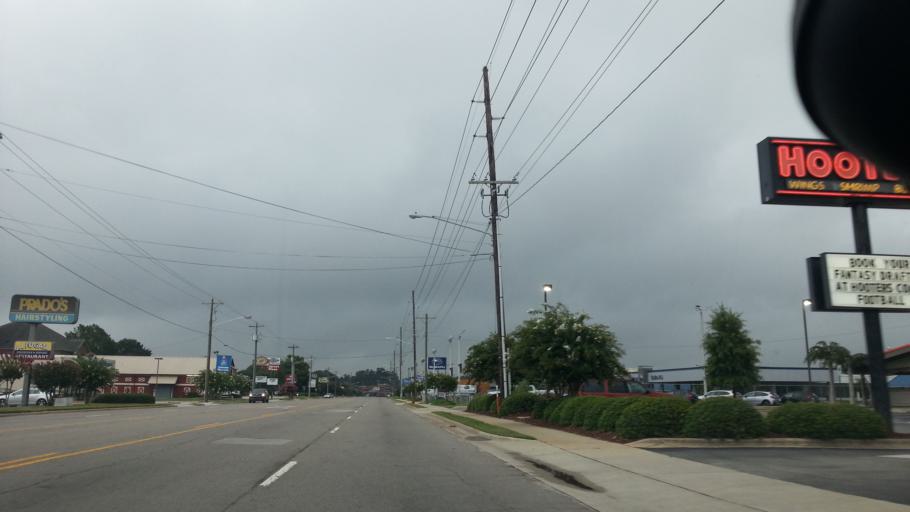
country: US
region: North Carolina
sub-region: Cumberland County
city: Fayetteville
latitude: 35.0739
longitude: -78.9532
